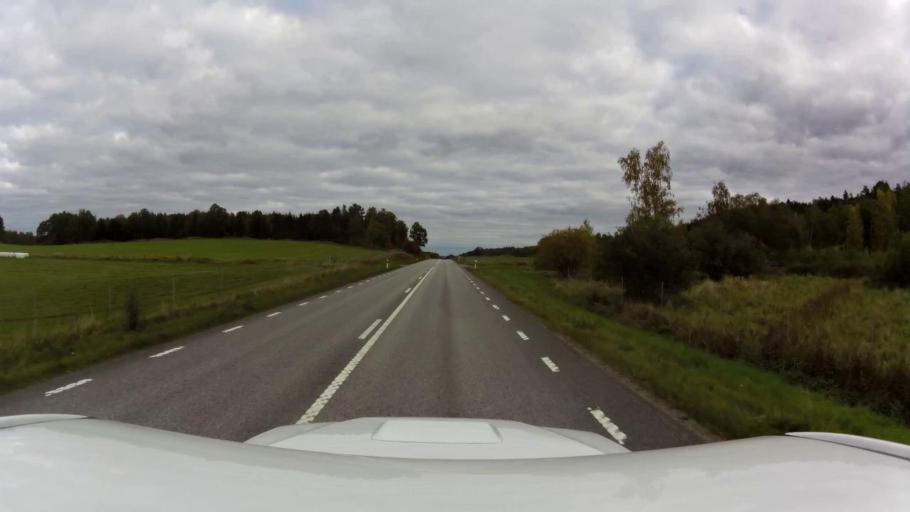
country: SE
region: OEstergoetland
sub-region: Kinda Kommun
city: Rimforsa
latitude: 58.1916
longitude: 15.6666
